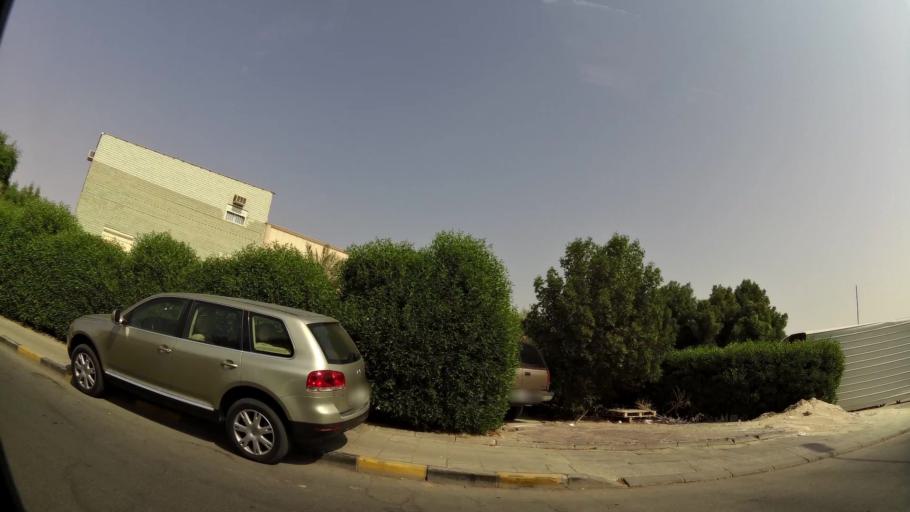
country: KW
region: Muhafazat al Jahra'
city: Al Jahra'
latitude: 29.3315
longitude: 47.6577
